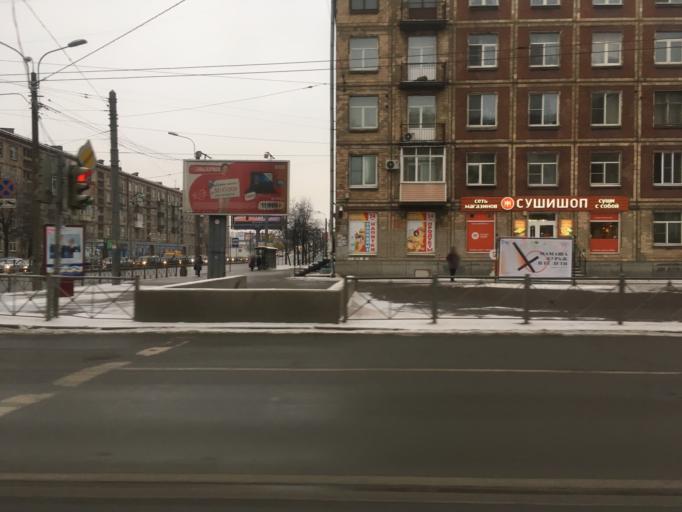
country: RU
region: St.-Petersburg
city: Obukhovo
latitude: 59.8735
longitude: 30.4370
